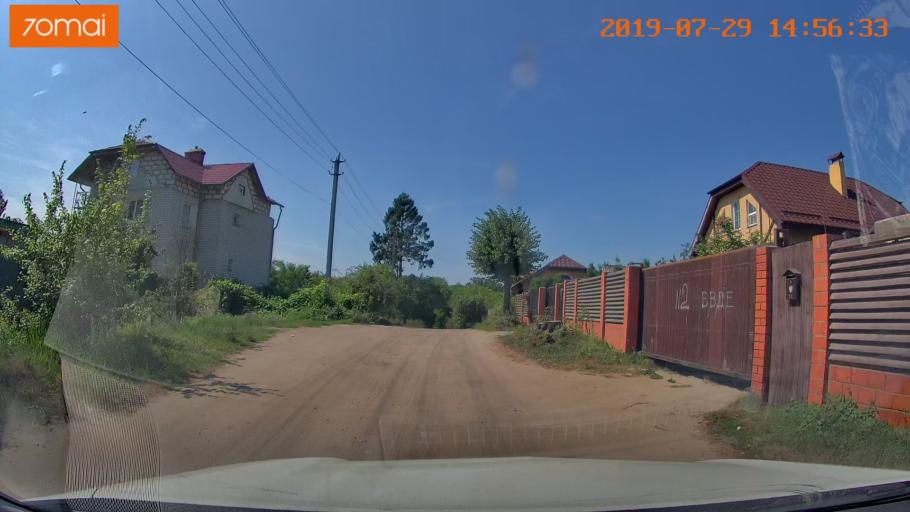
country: RU
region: Kaliningrad
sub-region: Gorod Kaliningrad
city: Baltiysk
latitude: 54.6801
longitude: 19.9200
